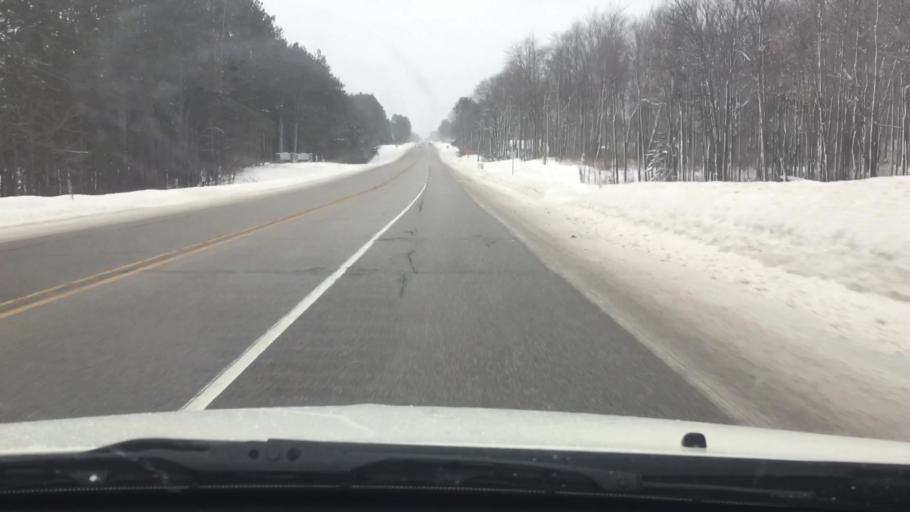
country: US
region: Michigan
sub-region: Otsego County
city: Gaylord
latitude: 45.0382
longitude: -84.7758
